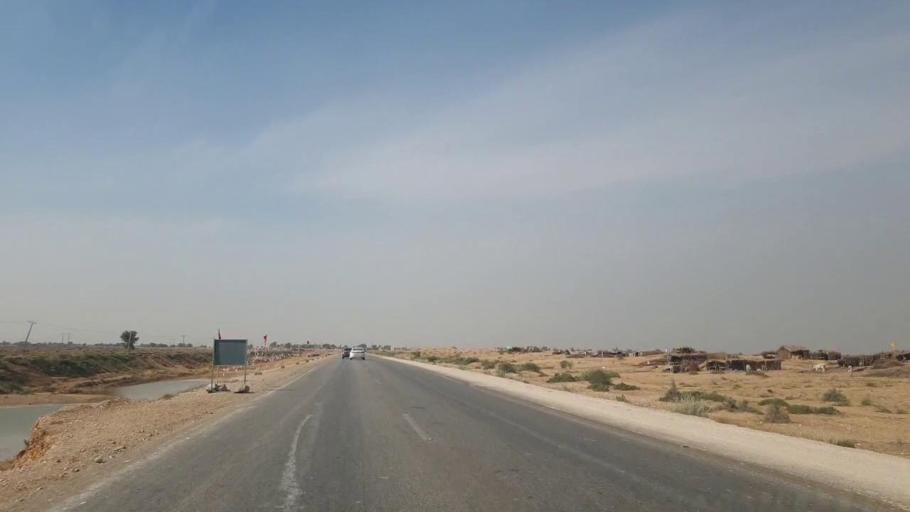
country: PK
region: Sindh
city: Sann
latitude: 26.0219
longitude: 68.1337
